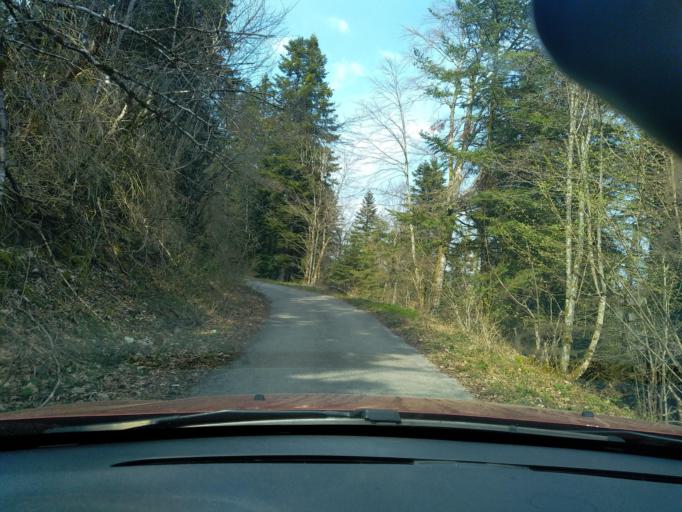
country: FR
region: Franche-Comte
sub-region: Departement du Jura
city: Moirans-en-Montagne
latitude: 46.4710
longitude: 5.7629
